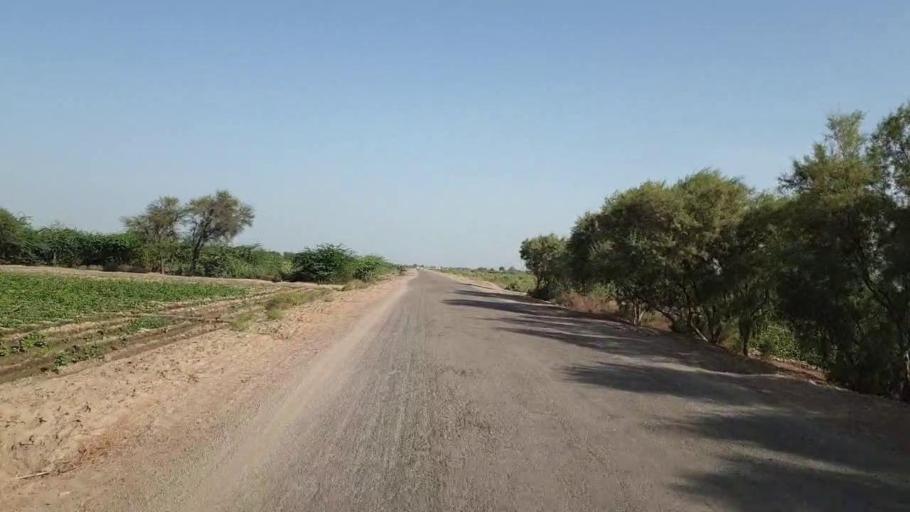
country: PK
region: Sindh
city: Nawabshah
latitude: 26.1538
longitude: 68.4466
